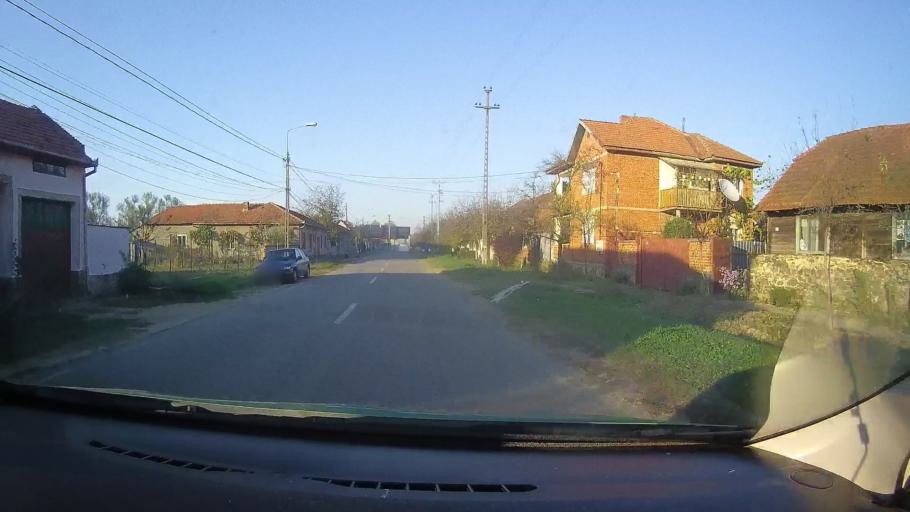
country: RO
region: Timis
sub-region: Comuna Fardea
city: Fardea
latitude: 45.7399
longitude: 22.1645
